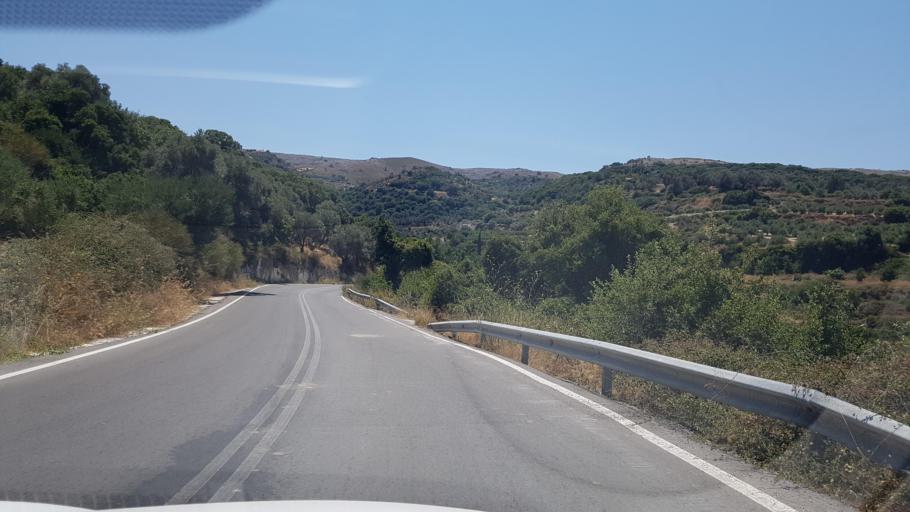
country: GR
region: Crete
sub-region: Nomos Rethymnis
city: Agia Foteini
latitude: 35.3368
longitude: 24.6104
